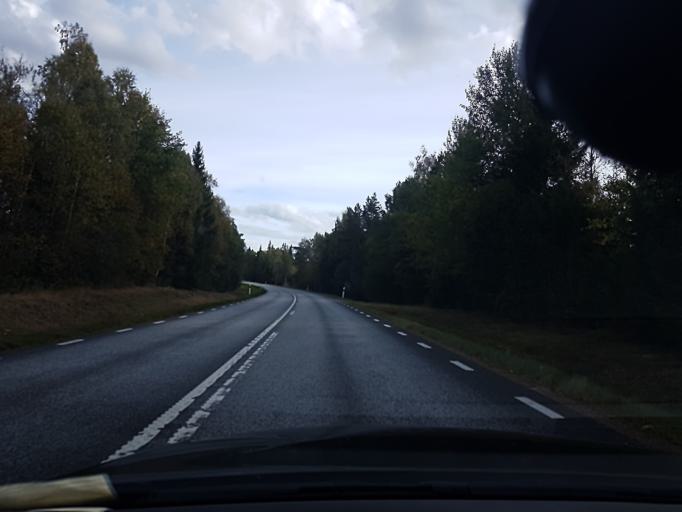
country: SE
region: Joenkoeping
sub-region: Varnamo Kommun
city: Bredaryd
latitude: 57.1887
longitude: 13.7253
